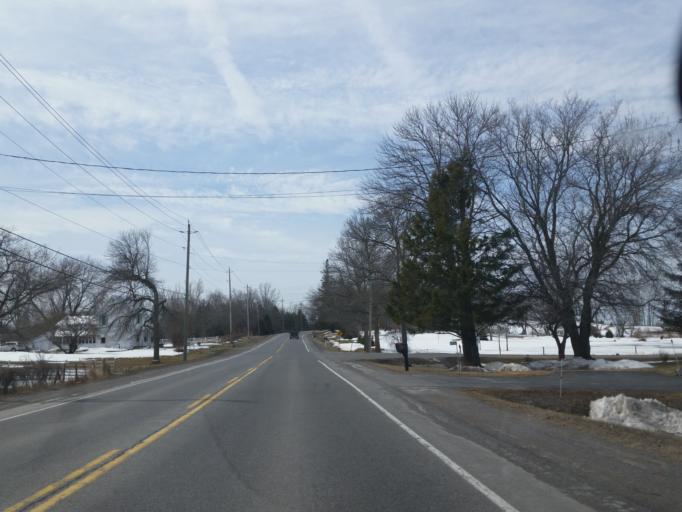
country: CA
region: Ontario
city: Napanee Downtown
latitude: 44.2152
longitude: -76.9859
